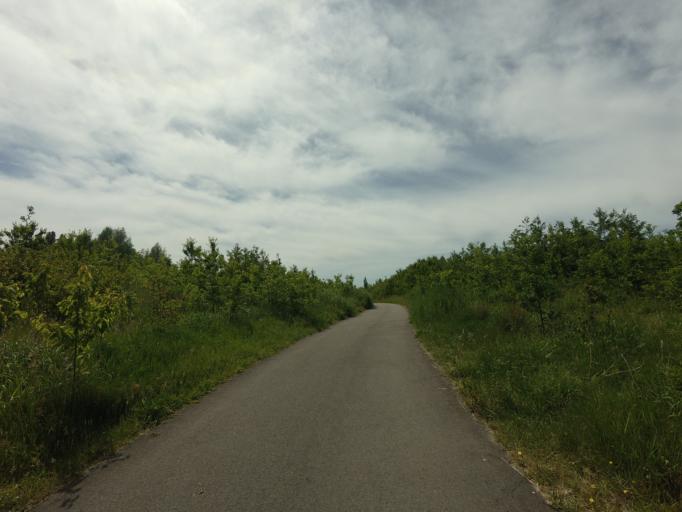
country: NL
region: Utrecht
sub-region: Stichtse Vecht
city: Spechtenkamp
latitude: 52.0928
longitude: 5.0257
